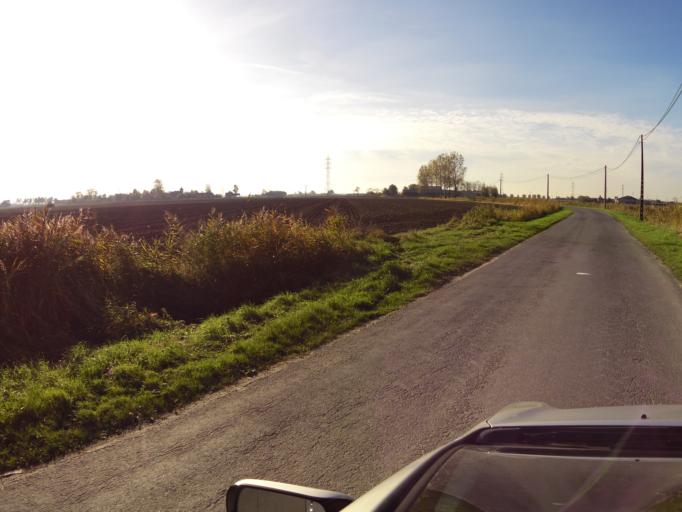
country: BE
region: Flanders
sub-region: Provincie West-Vlaanderen
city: Nieuwpoort
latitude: 51.0917
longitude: 2.7497
